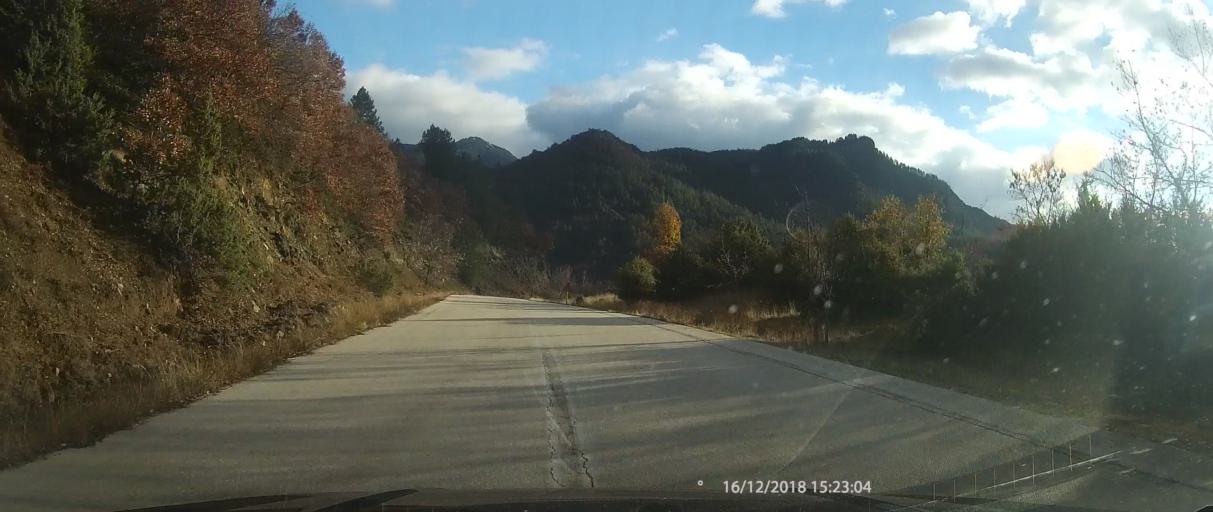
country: GR
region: Epirus
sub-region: Nomos Ioanninon
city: Konitsa
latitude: 40.1486
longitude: 20.8090
